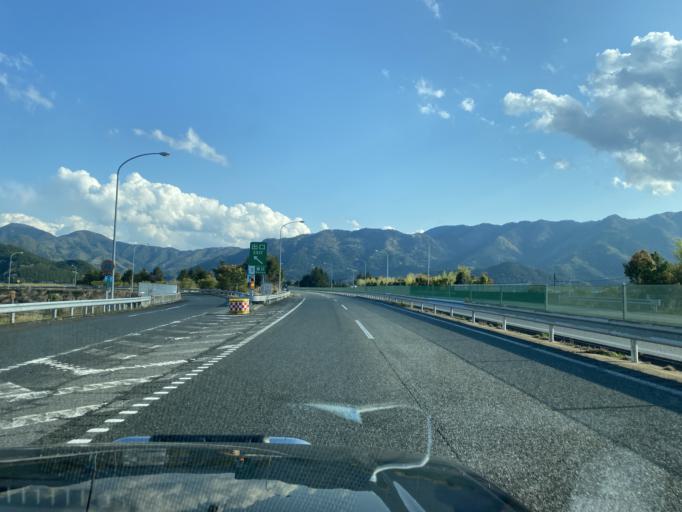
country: JP
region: Kyoto
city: Fukuchiyama
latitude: 35.1675
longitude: 135.1190
